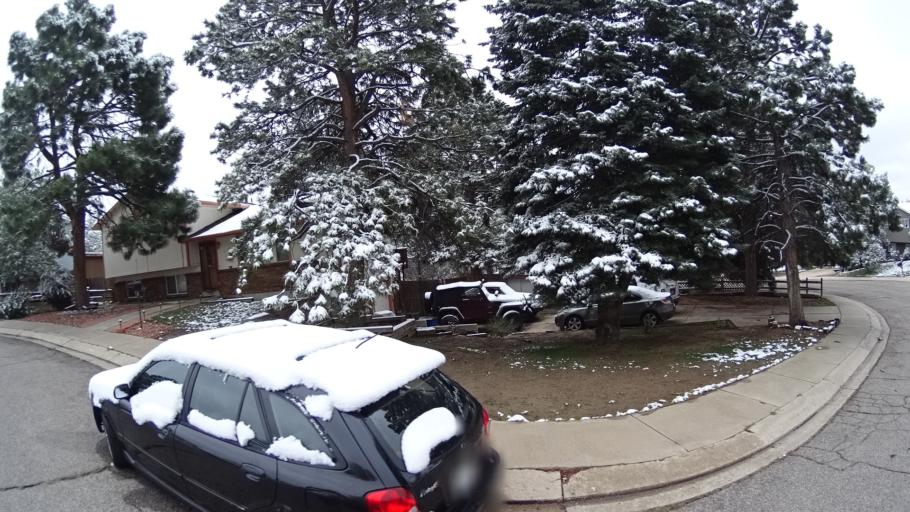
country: US
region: Colorado
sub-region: El Paso County
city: Cimarron Hills
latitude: 38.9090
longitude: -104.7628
